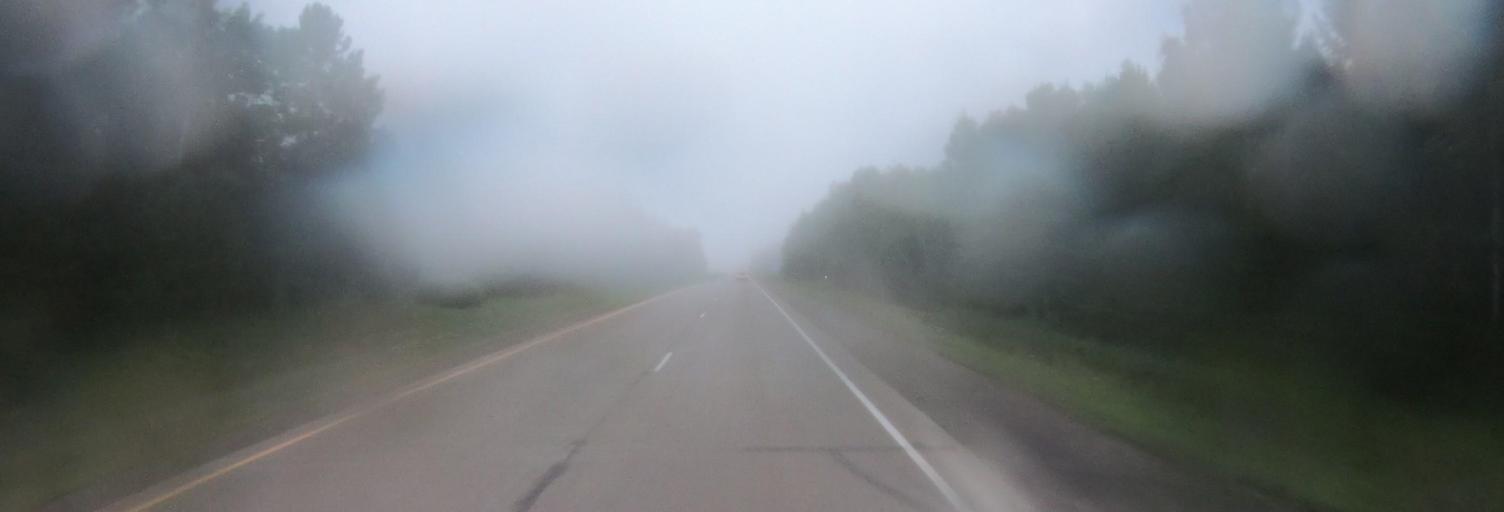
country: US
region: Minnesota
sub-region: Carlton County
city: Moose Lake
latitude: 46.5426
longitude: -92.6187
